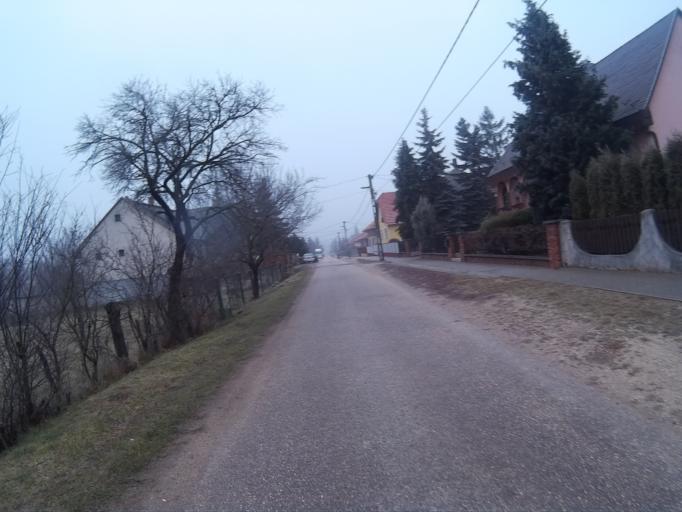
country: HU
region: Fejer
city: Zamoly
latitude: 47.3886
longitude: 18.3854
